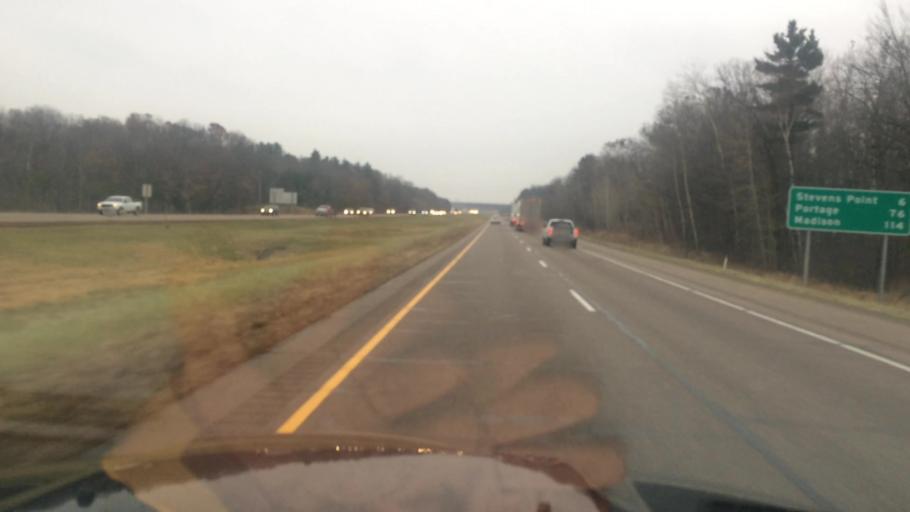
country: US
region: Wisconsin
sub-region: Portage County
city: Stevens Point
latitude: 44.5866
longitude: -89.6091
